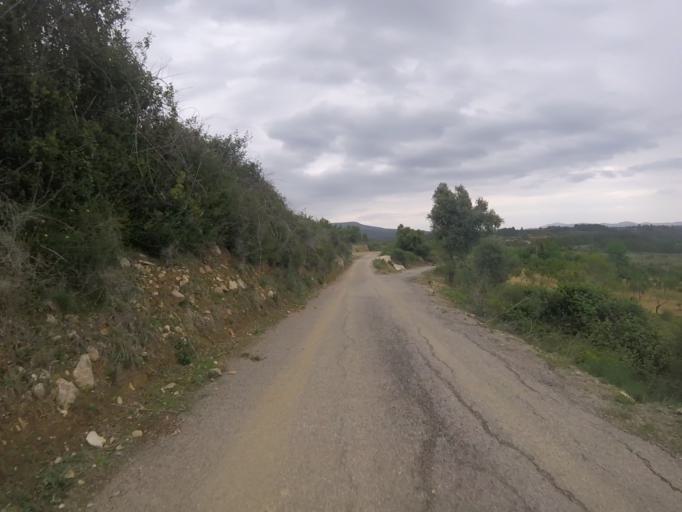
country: ES
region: Valencia
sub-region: Provincia de Castello
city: Sarratella
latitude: 40.2668
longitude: 0.0697
